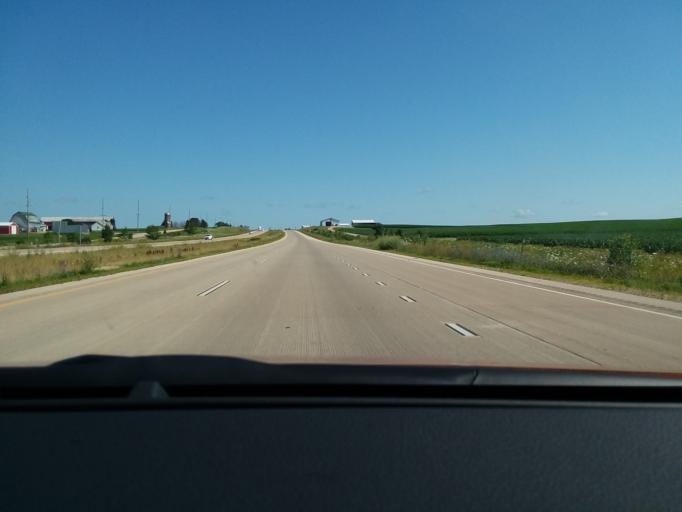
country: US
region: Wisconsin
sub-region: Dane County
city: Windsor
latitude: 43.2222
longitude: -89.3226
